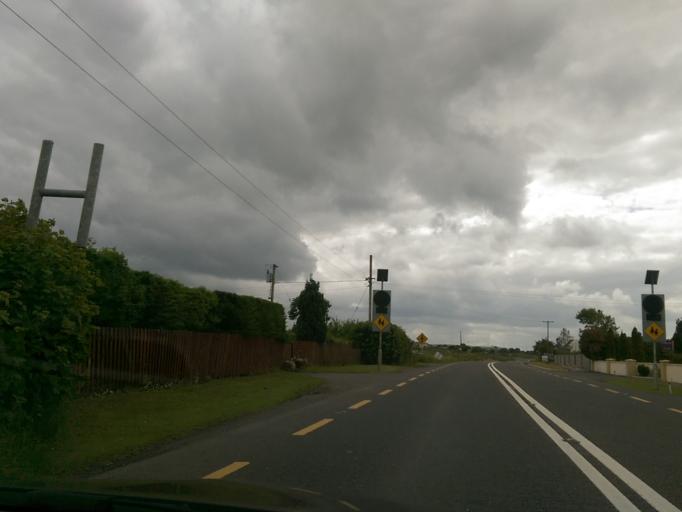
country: IE
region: Munster
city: Thurles
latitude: 52.6334
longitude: -7.7790
